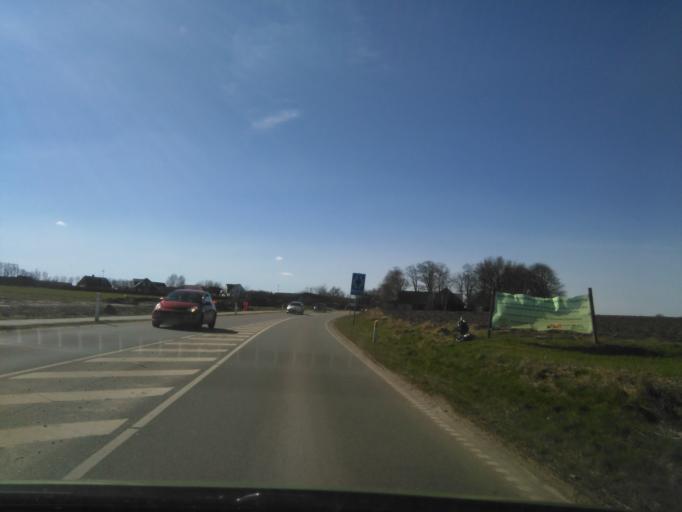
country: DK
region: Central Jutland
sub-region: Favrskov Kommune
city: Hinnerup
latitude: 56.2477
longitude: 10.0524
